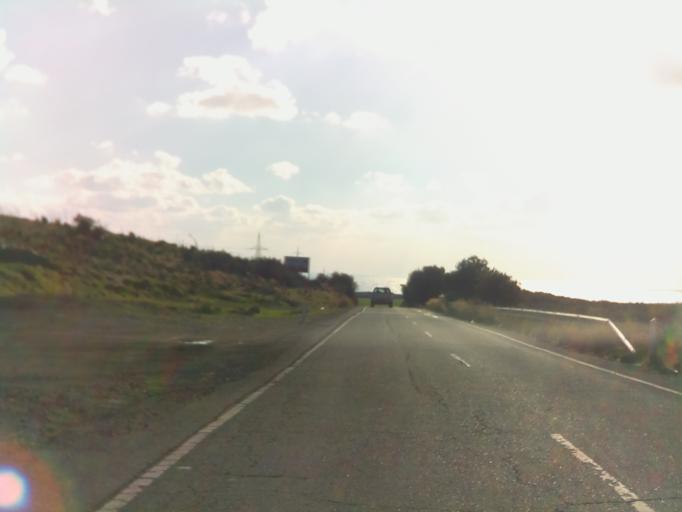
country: CY
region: Pafos
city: Mesogi
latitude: 34.7596
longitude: 32.5255
